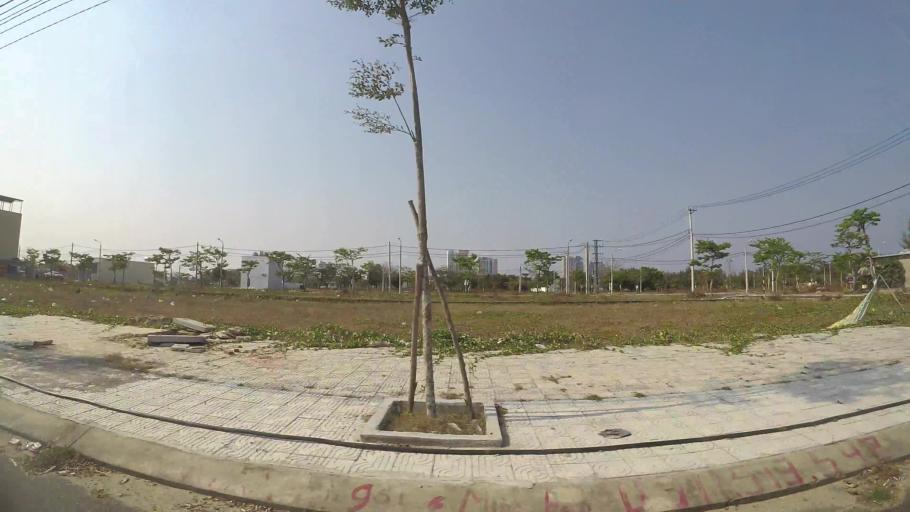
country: VN
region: Da Nang
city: Ngu Hanh Son
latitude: 15.9543
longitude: 108.2814
